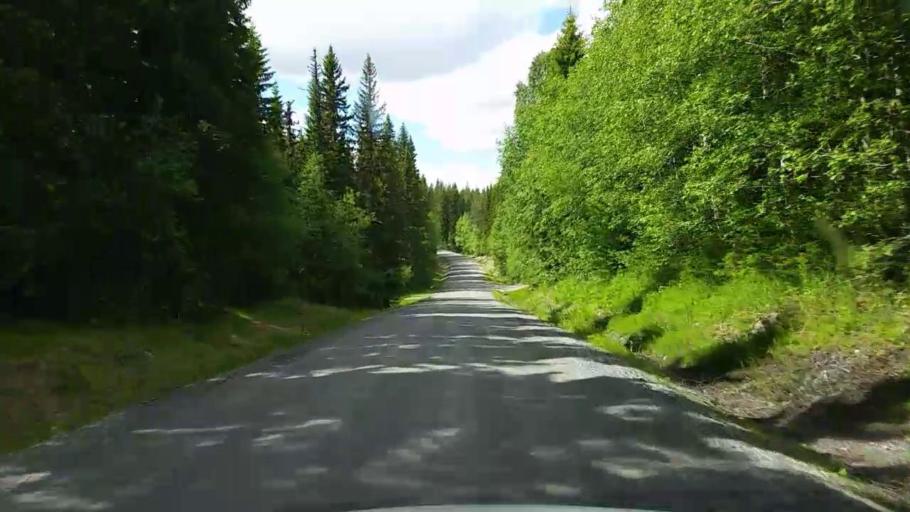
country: SE
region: Gaevleborg
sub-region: Bollnas Kommun
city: Vittsjo
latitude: 61.0897
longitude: 16.2055
